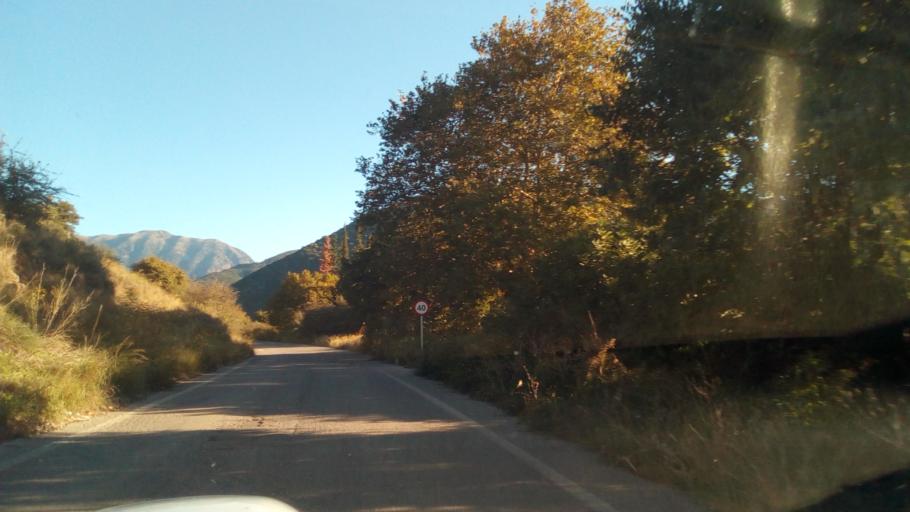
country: GR
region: West Greece
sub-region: Nomos Aitolias kai Akarnanias
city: Nafpaktos
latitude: 38.4202
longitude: 21.8780
